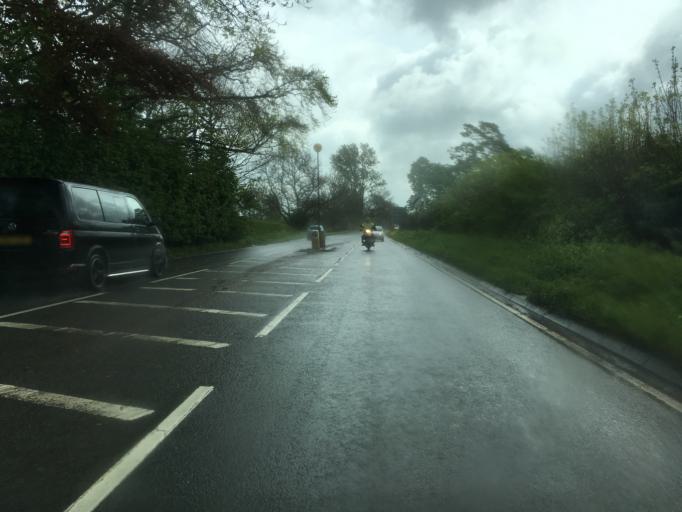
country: GB
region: England
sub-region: North Somerset
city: Churchill
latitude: 51.3396
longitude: -2.7811
